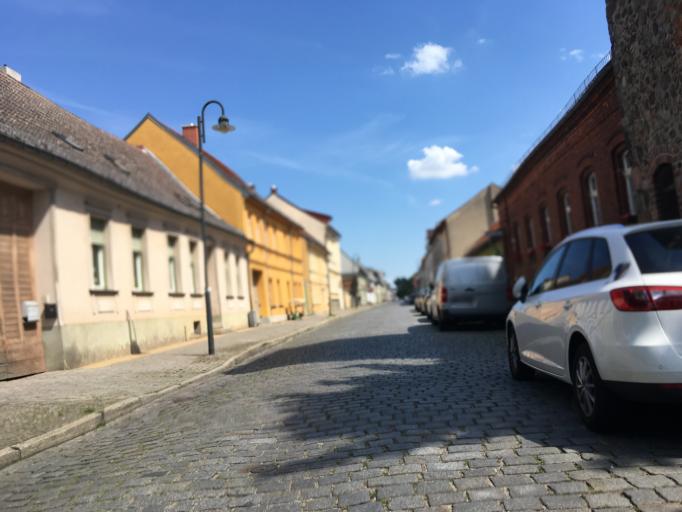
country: DE
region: Brandenburg
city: Altlandsberg
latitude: 52.5625
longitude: 13.7235
